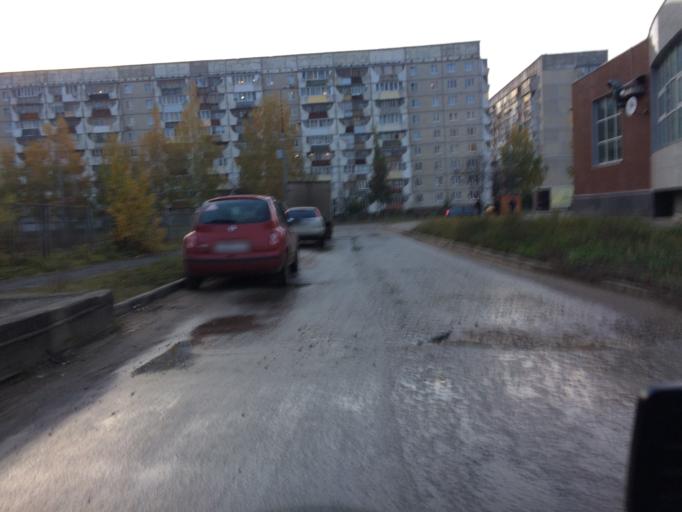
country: RU
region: Mariy-El
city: Yoshkar-Ola
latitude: 56.6323
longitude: 47.9203
